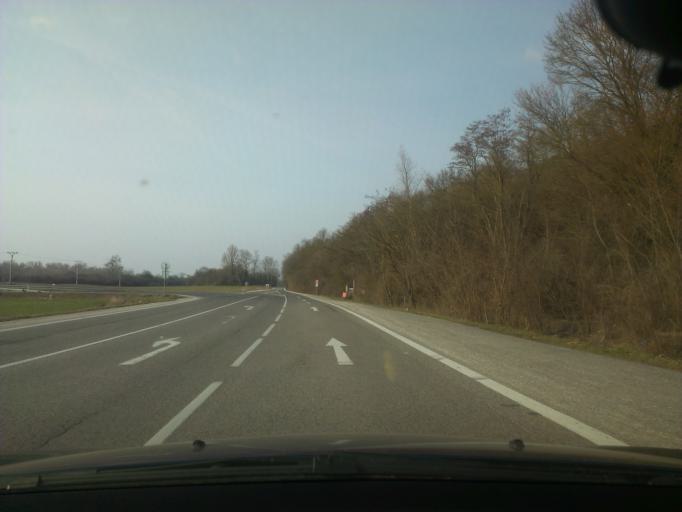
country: SK
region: Trnavsky
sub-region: Okres Trnava
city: Piestany
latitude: 48.6724
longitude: 17.8754
